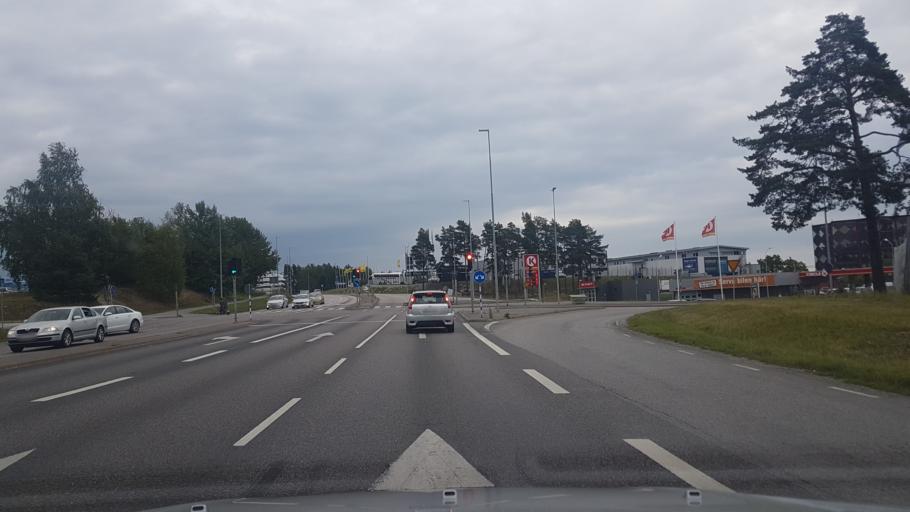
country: SE
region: Stockholm
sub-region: Jarfalla Kommun
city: Jakobsberg
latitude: 59.4070
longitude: 17.8407
